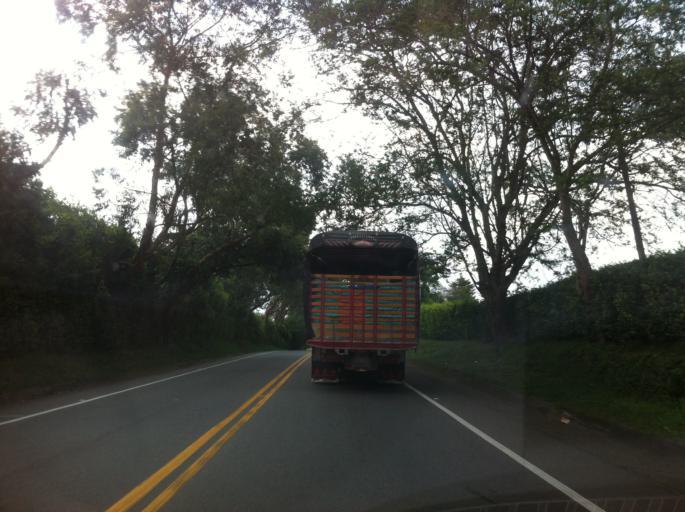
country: CO
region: Quindio
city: La Tebaida
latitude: 4.4478
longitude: -75.8216
